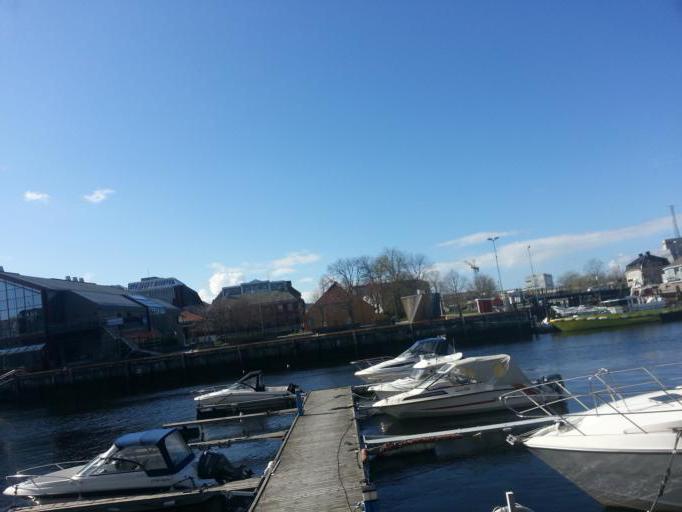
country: NO
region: Sor-Trondelag
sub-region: Trondheim
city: Trondheim
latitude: 63.4341
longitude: 10.4080
